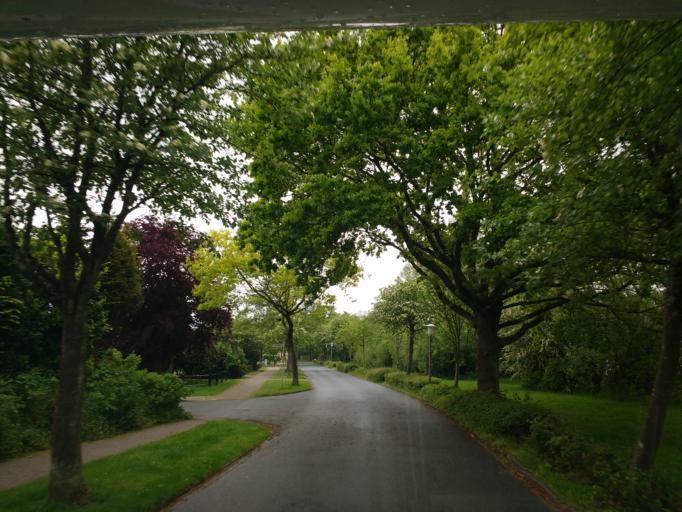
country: DE
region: Lower Saxony
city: Schillig
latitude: 53.7042
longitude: 8.0217
